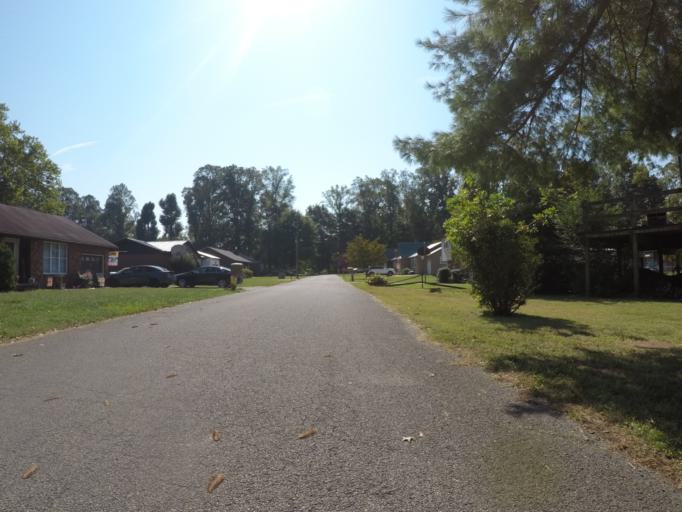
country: US
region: West Virginia
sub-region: Cabell County
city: Barboursville
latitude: 38.3703
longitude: -82.2724
